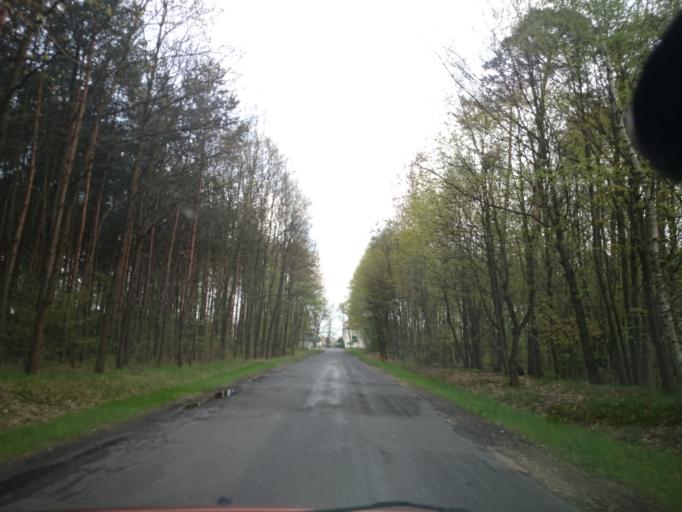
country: PL
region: Opole Voivodeship
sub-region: Powiat strzelecki
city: Izbicko
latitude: 50.5521
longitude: 18.1433
